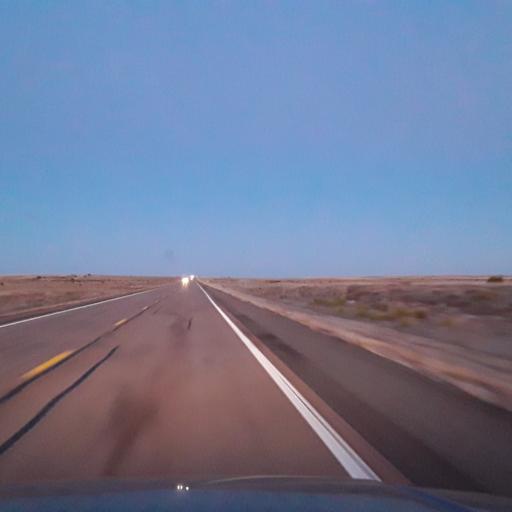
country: US
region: New Mexico
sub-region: Guadalupe County
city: Santa Rosa
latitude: 34.7612
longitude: -104.9877
